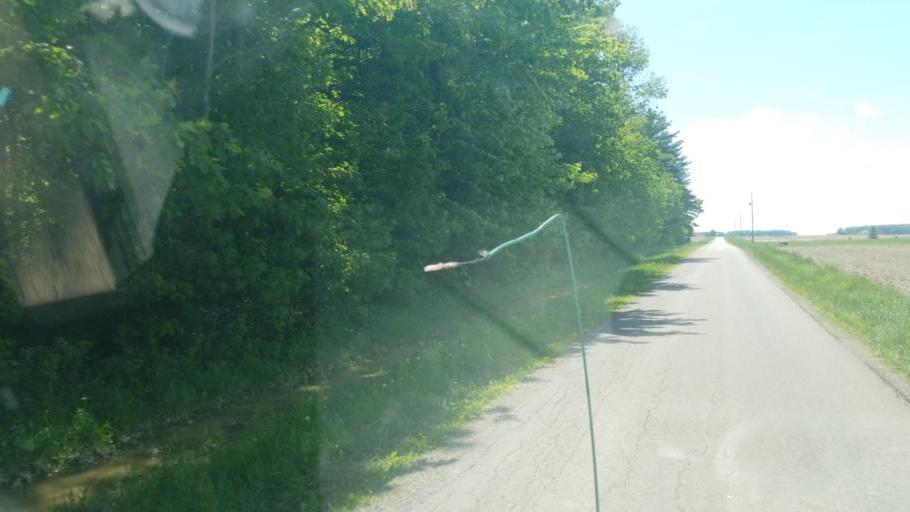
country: US
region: Ohio
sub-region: Crawford County
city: Bucyrus
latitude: 40.9795
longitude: -83.0078
